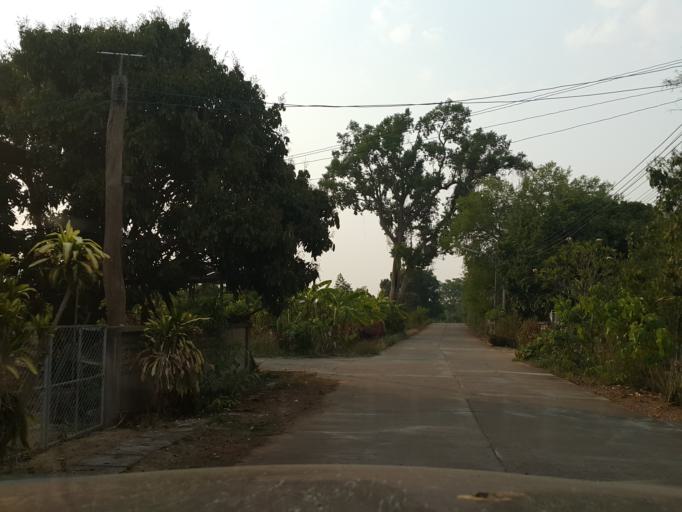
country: TH
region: Lamphun
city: Li
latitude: 17.8067
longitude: 98.9501
